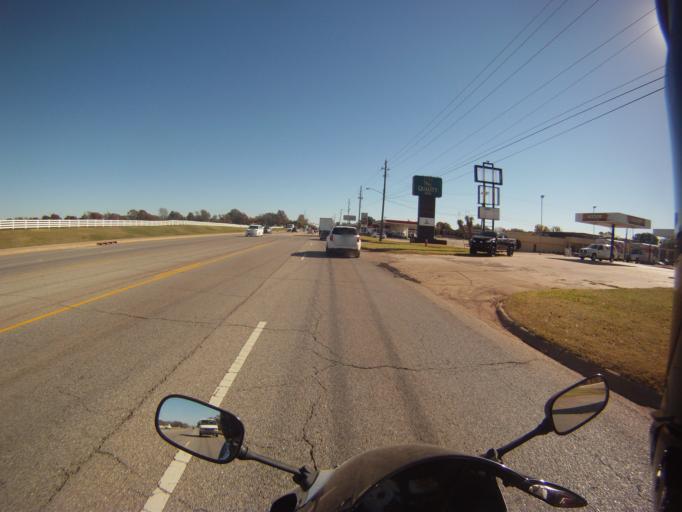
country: US
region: Oklahoma
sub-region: Payne County
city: Stillwater
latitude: 36.1157
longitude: -97.0917
